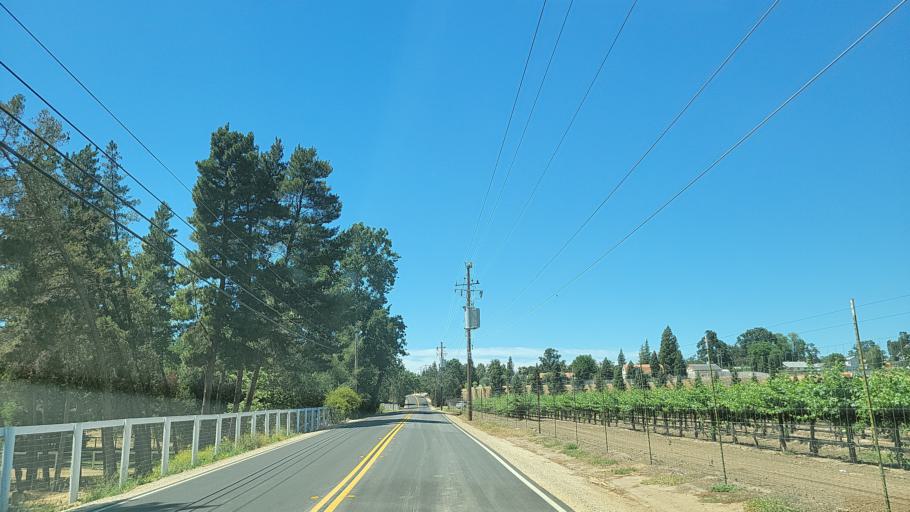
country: US
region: California
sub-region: San Luis Obispo County
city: Atascadero
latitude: 35.4980
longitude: -120.6471
